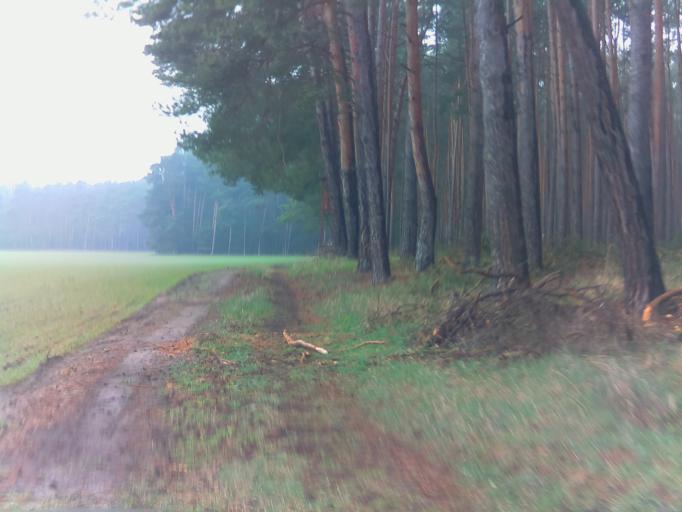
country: DE
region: Brandenburg
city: Neu Zauche
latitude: 51.9699
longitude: 14.1085
